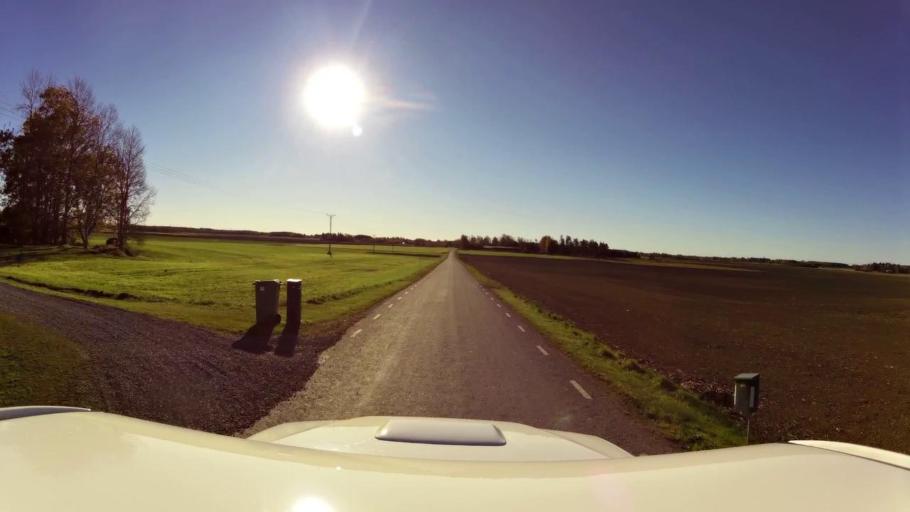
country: SE
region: OEstergoetland
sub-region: Linkopings Kommun
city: Ljungsbro
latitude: 58.5057
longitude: 15.4178
